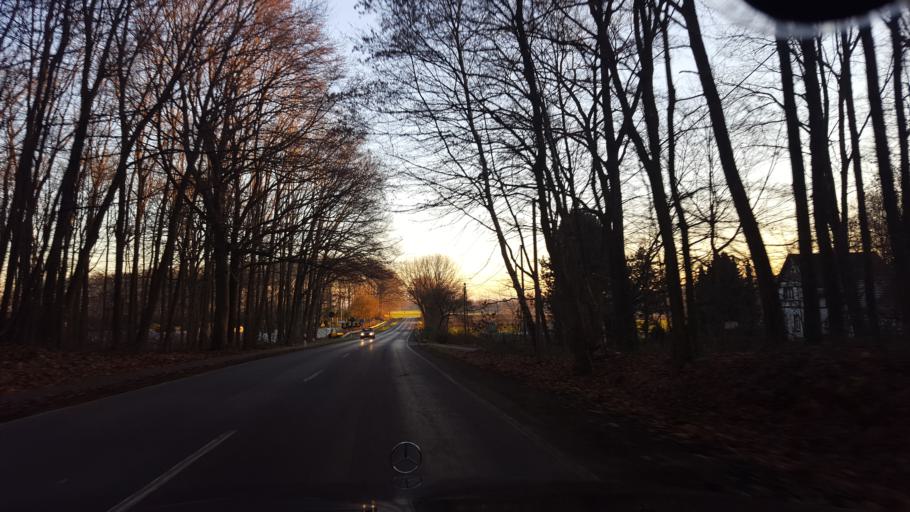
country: DE
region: North Rhine-Westphalia
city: Oer-Erkenschwick
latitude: 51.6606
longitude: 7.2704
